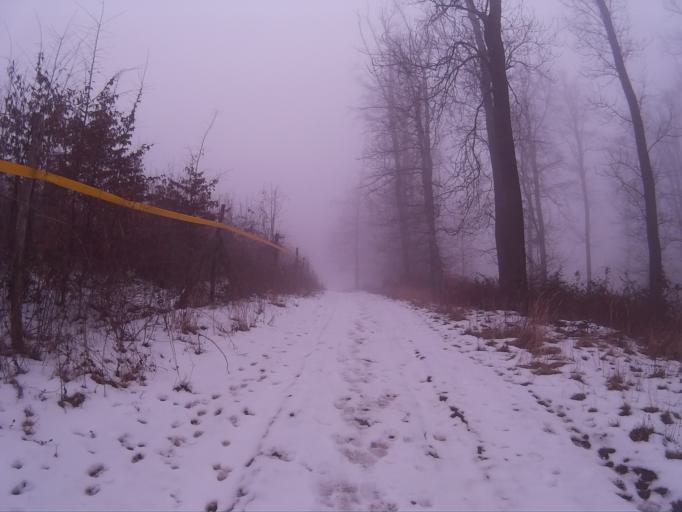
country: HU
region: Komarom-Esztergom
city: Tardos
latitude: 47.6859
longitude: 18.4917
